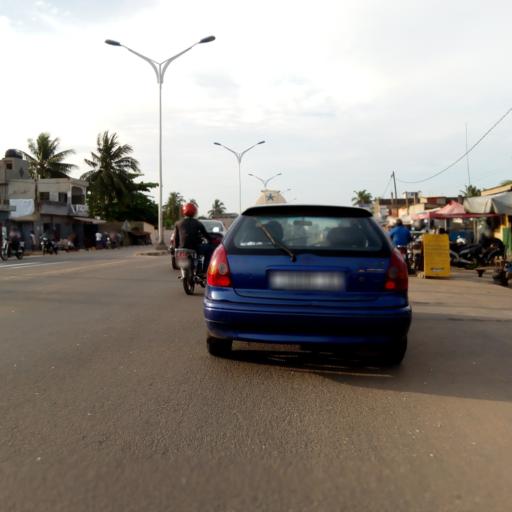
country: TG
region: Maritime
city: Lome
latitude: 6.1657
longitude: 1.2834
